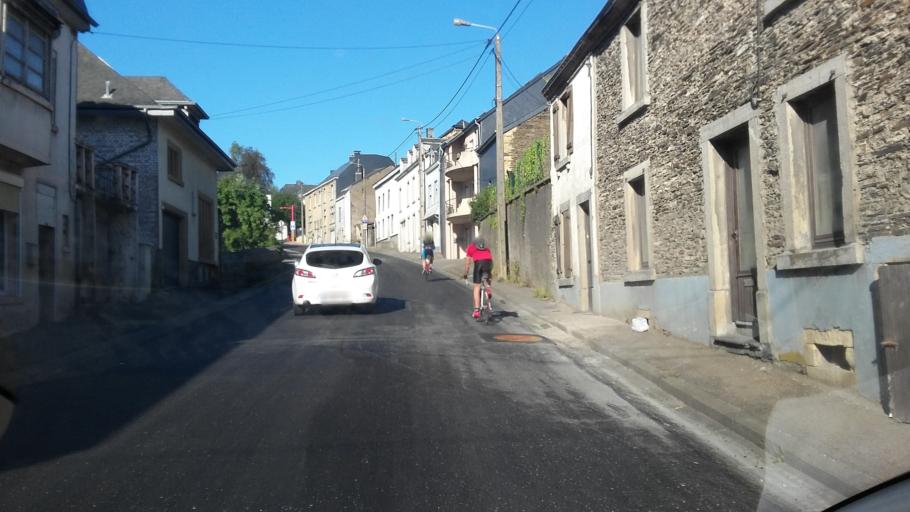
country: BE
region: Wallonia
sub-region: Province du Luxembourg
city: Neufchateau
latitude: 49.8398
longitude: 5.4382
